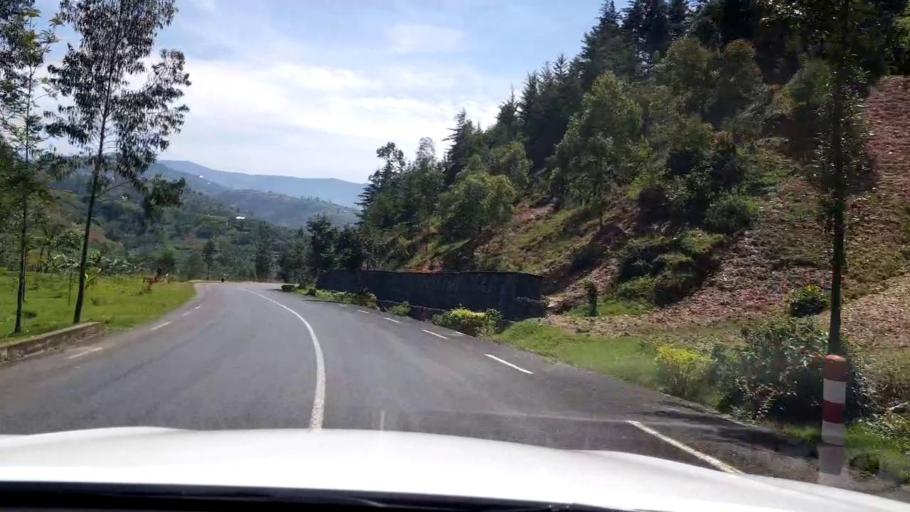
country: RW
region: Southern Province
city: Gitarama
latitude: -1.9188
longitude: 29.6327
